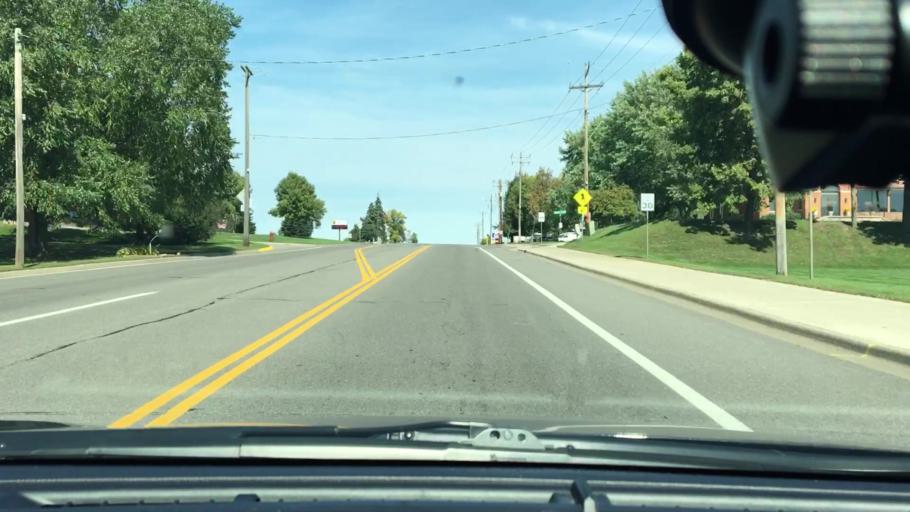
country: US
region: Minnesota
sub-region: Wright County
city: Hanover
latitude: 45.1554
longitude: -93.6660
